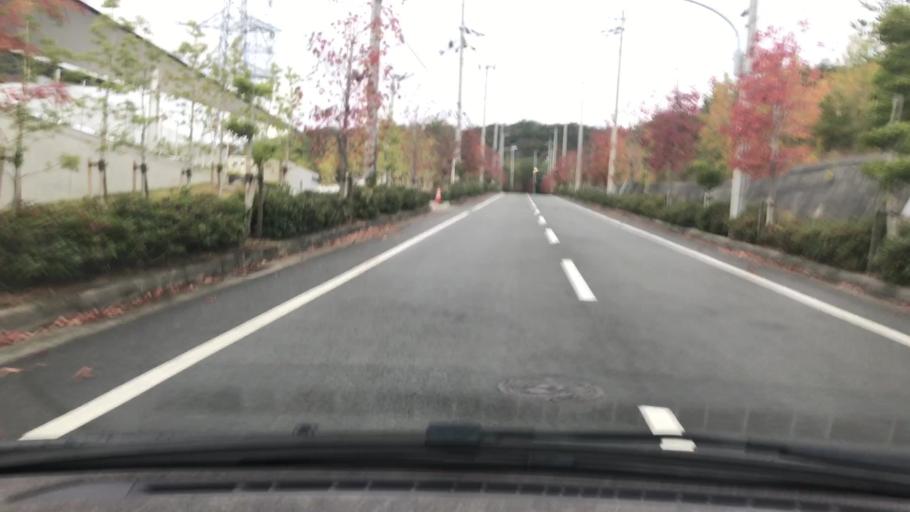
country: JP
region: Hyogo
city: Takarazuka
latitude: 34.8360
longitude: 135.3008
